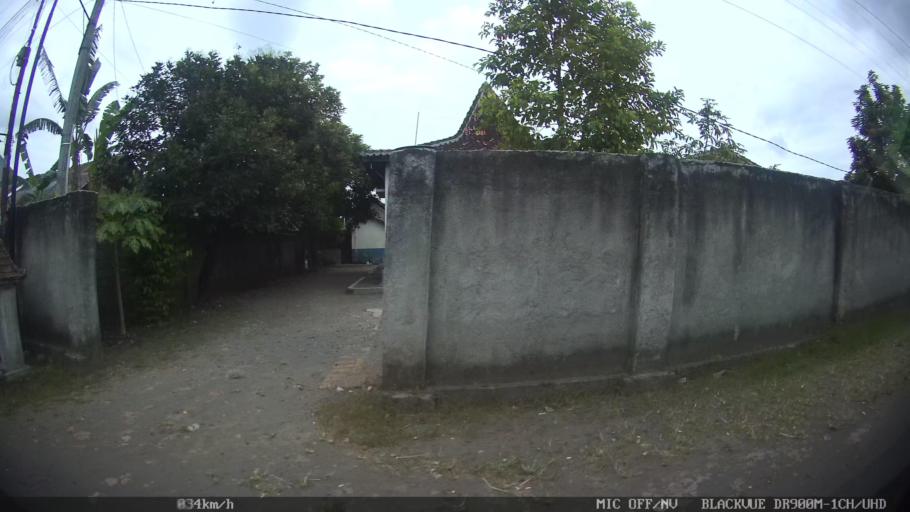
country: ID
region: Daerah Istimewa Yogyakarta
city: Sewon
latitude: -7.8714
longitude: 110.4167
